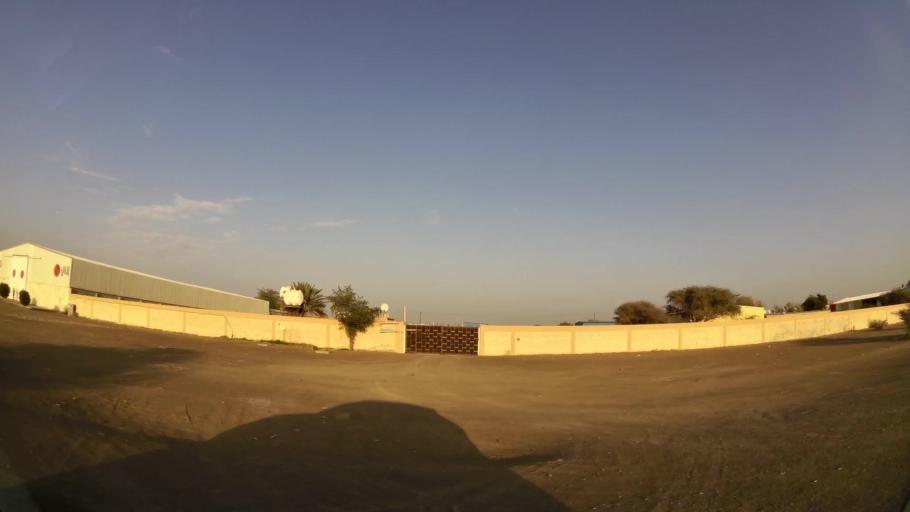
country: AE
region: Abu Dhabi
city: Al Ain
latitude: 24.1567
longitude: 55.8220
